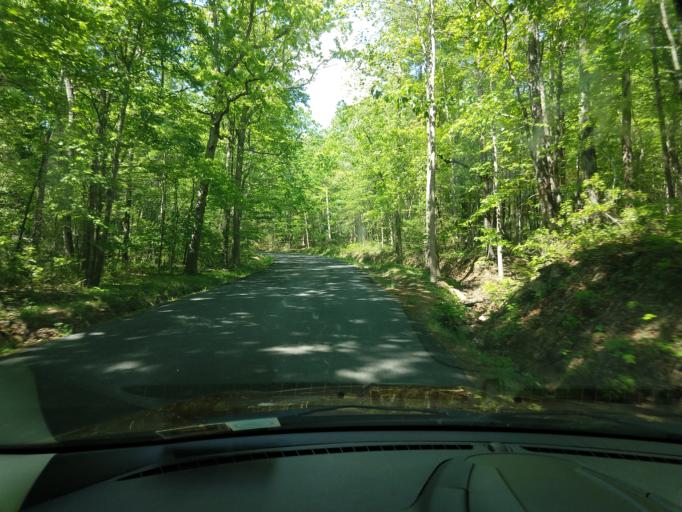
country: US
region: Virginia
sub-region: City of Covington
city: Fairlawn
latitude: 37.7077
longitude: -79.8886
